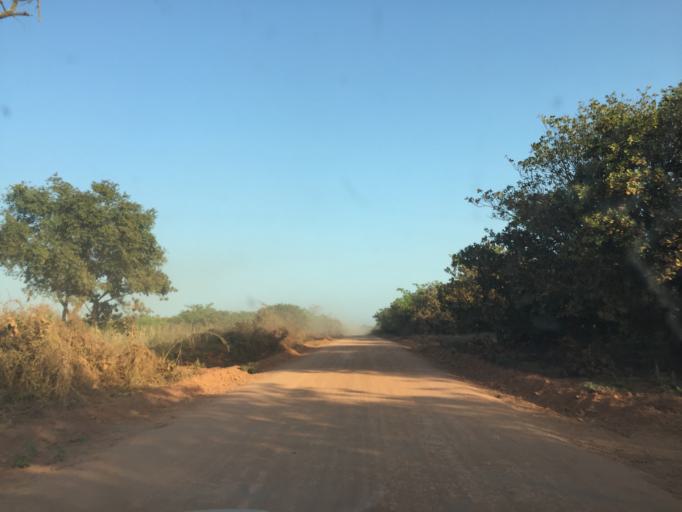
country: GW
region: Oio
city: Farim
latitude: 12.5302
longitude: -15.2710
